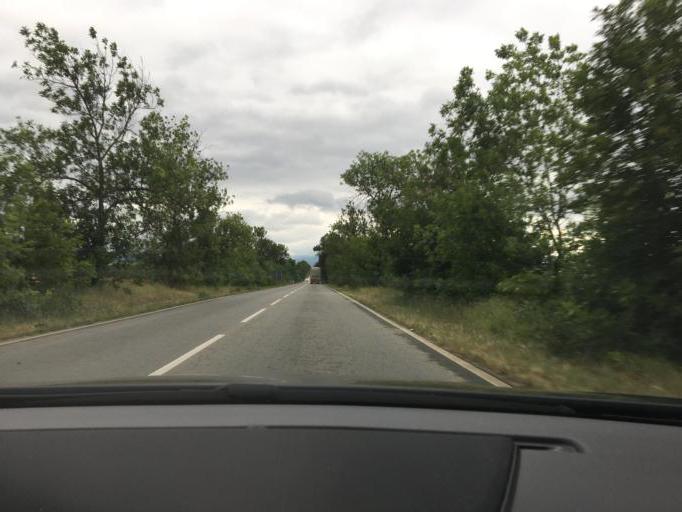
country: BG
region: Kyustendil
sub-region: Obshtina Kyustendil
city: Kyustendil
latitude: 42.2703
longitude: 22.7856
